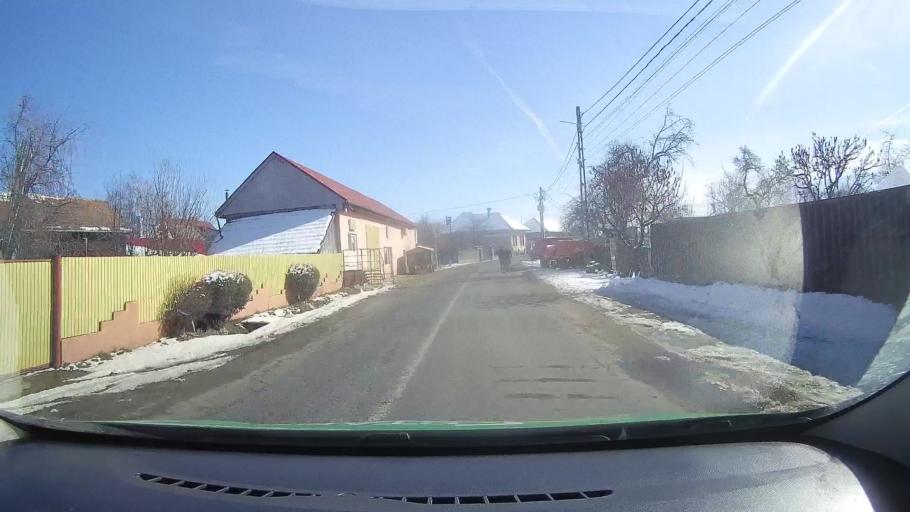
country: RO
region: Brasov
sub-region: Comuna Recea
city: Recea
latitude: 45.7324
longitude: 24.9421
